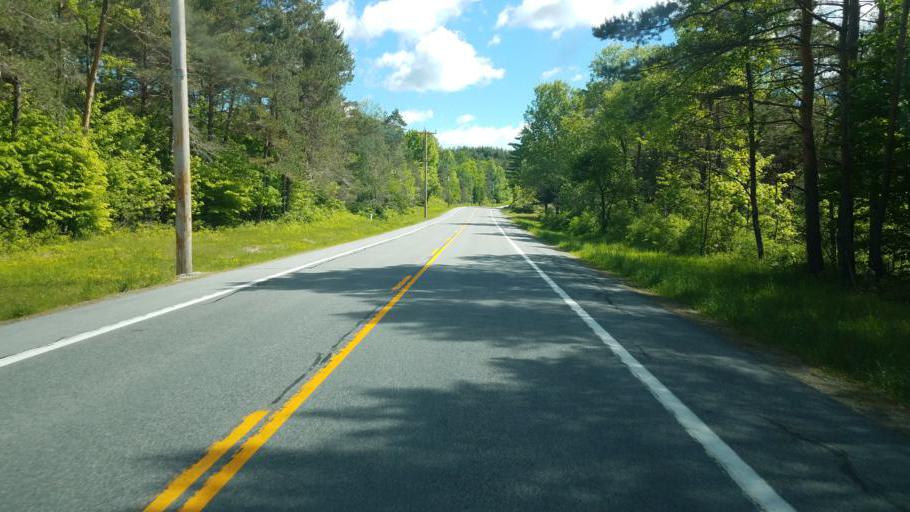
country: US
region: New York
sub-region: Oneida County
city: Boonville
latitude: 43.4748
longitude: -75.1746
